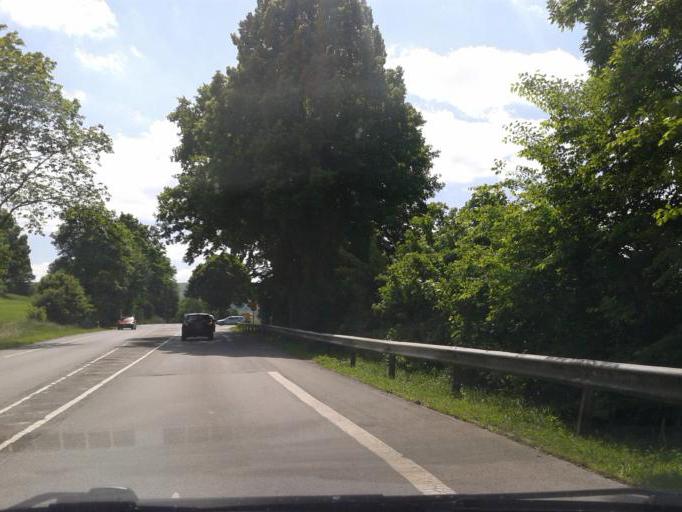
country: DE
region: North Rhine-Westphalia
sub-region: Regierungsbezirk Detmold
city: Lugde
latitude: 51.9376
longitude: 9.2352
